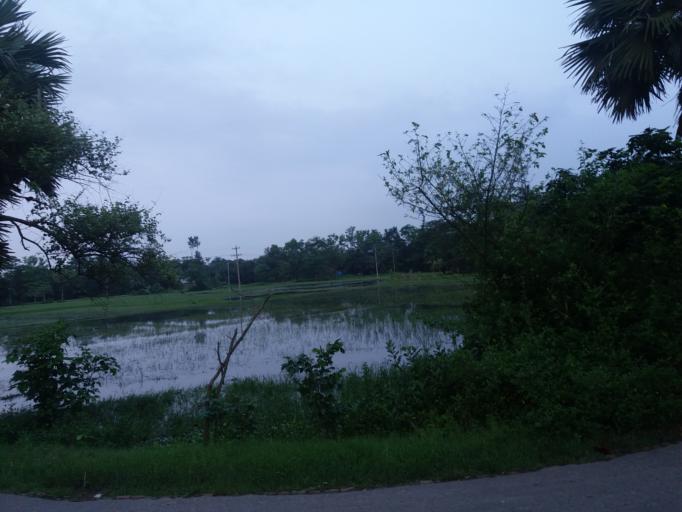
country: BD
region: Chittagong
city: Feni
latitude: 22.9302
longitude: 91.3375
